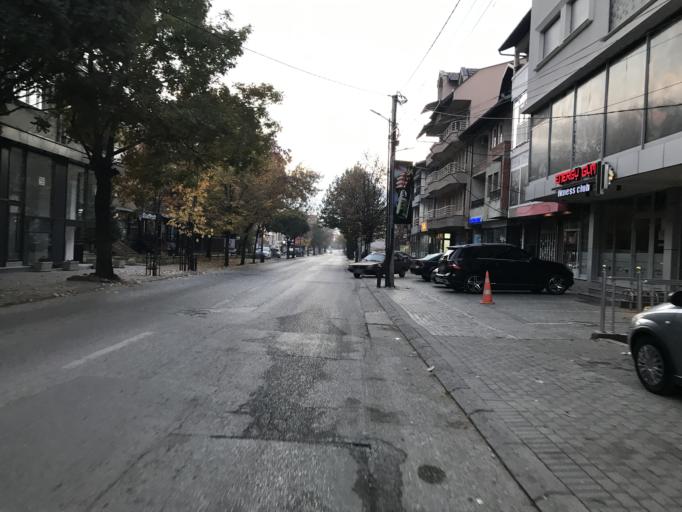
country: XK
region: Pec
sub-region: Komuna e Pejes
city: Peje
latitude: 42.6614
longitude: 20.3000
